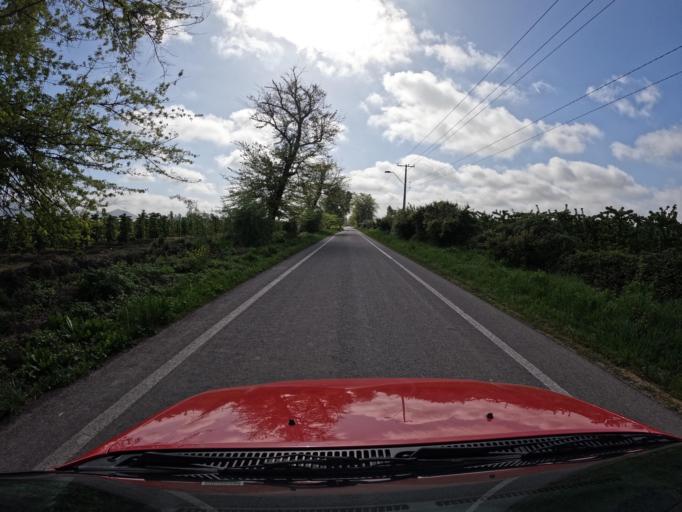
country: CL
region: Maule
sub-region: Provincia de Curico
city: Teno
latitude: -34.8804
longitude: -71.2380
